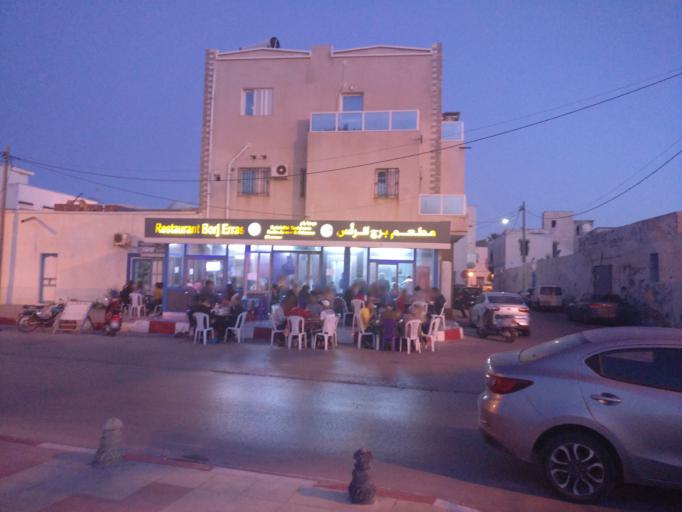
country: TN
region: Al Mahdiyah
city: Mahdia
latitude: 35.5052
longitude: 11.0668
